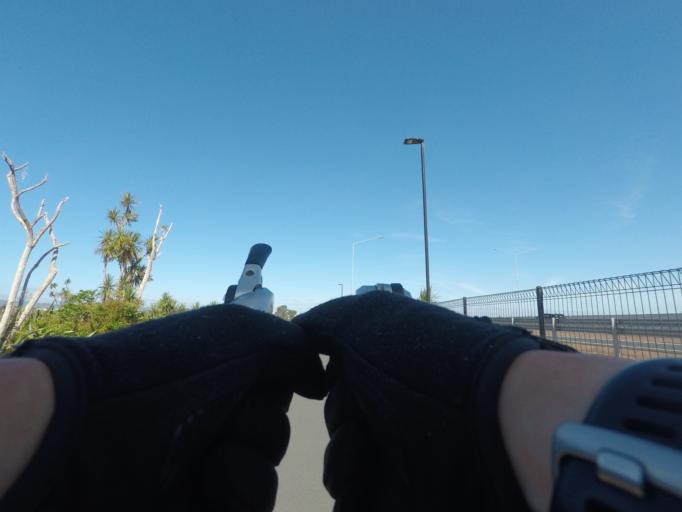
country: NZ
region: Auckland
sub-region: Auckland
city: Rosebank
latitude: -36.8721
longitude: 174.6802
